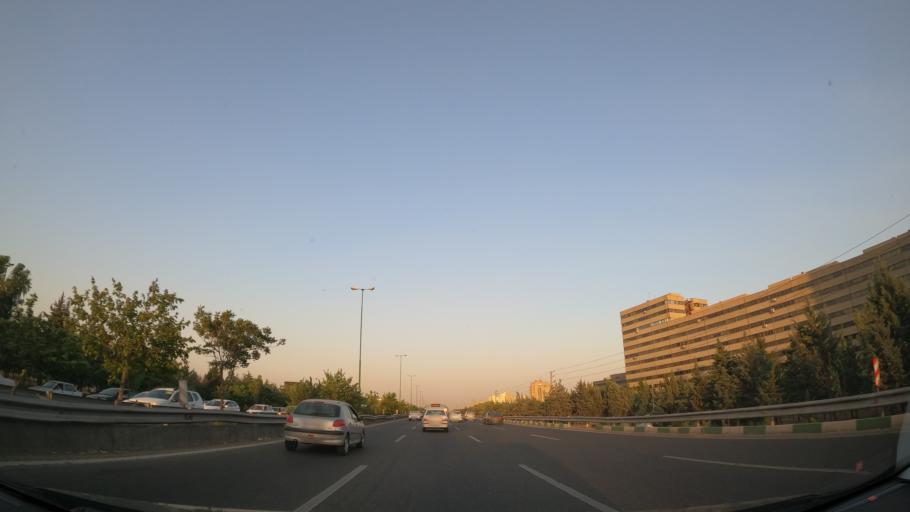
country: IR
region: Tehran
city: Tehran
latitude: 35.7159
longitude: 51.3181
